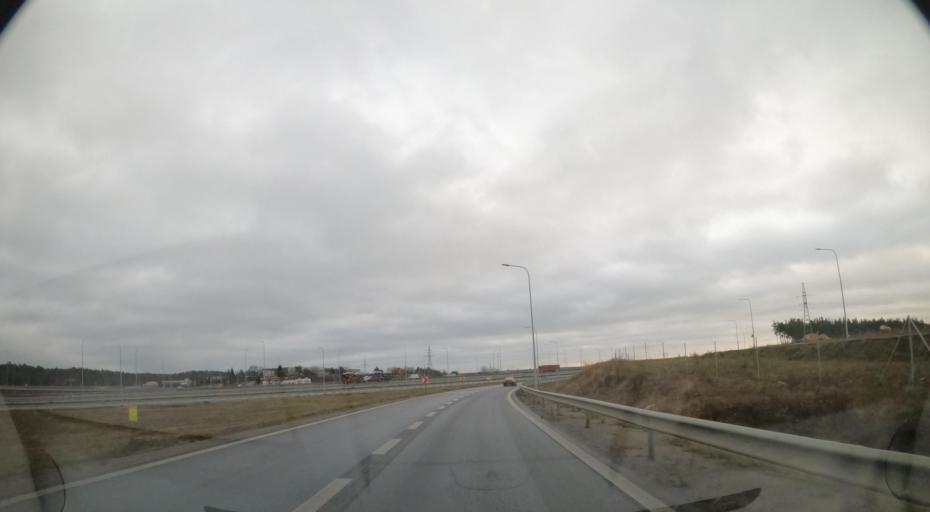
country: PL
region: Kujawsko-Pomorskie
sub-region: Powiat bydgoski
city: Biale Blota
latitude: 53.1557
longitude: 17.8845
